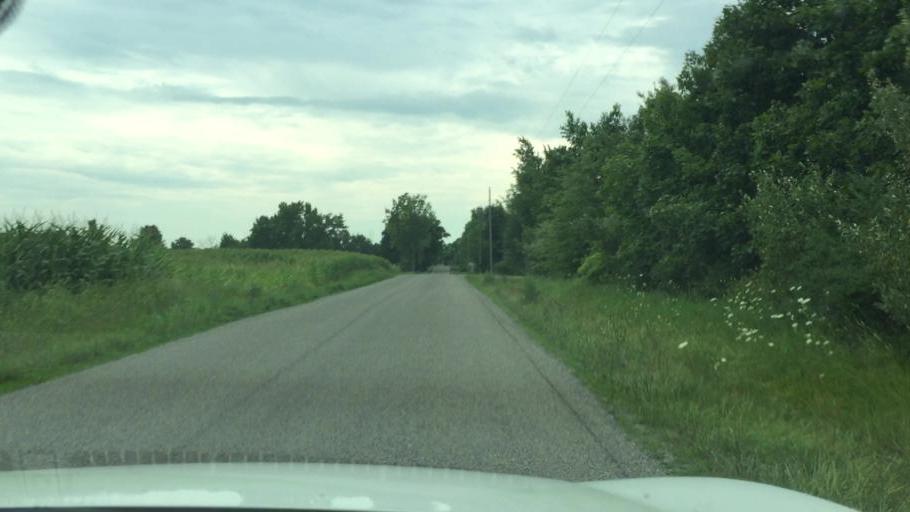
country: US
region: Ohio
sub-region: Champaign County
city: North Lewisburg
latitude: 40.2559
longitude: -83.5116
